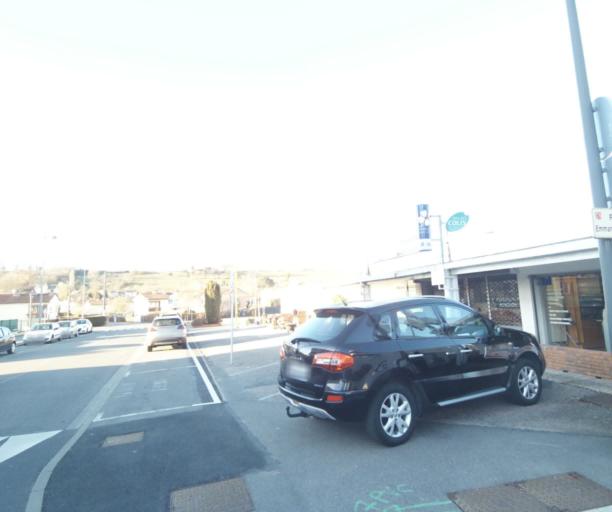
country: FR
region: Lorraine
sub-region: Departement de Meurthe-et-Moselle
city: Seichamps
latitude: 48.7148
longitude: 6.2602
